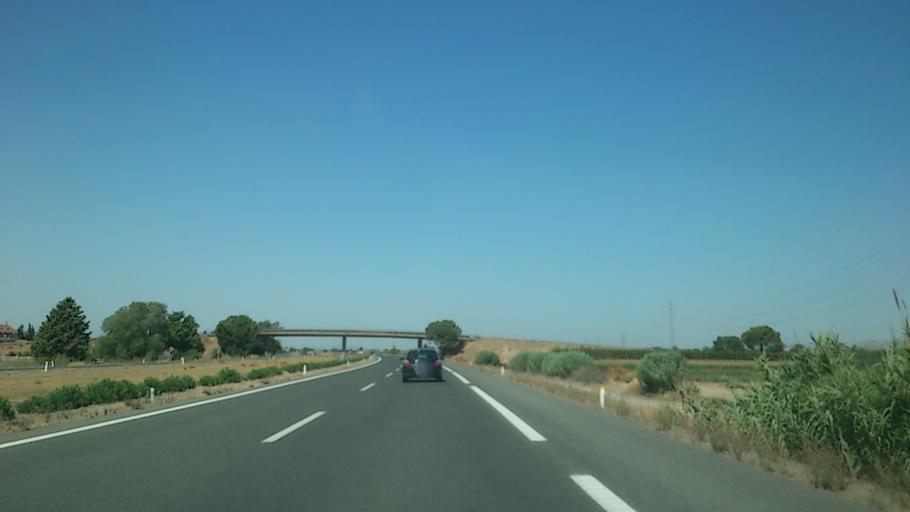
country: ES
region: Aragon
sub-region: Provincia de Zaragoza
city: Utebo
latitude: 41.7176
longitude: -0.9915
